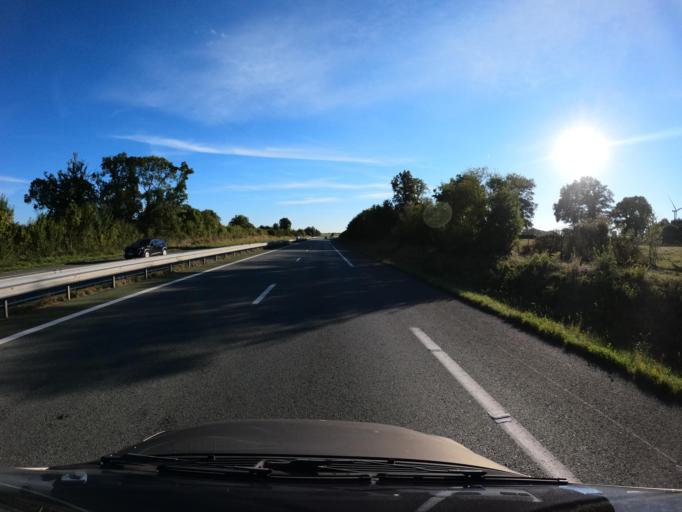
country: FR
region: Pays de la Loire
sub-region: Departement de Maine-et-Loire
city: Chemille-Melay
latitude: 47.1924
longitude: -0.7753
